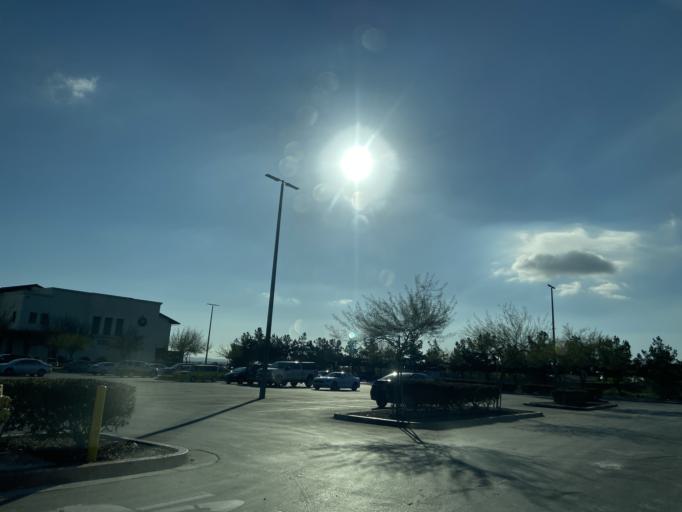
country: US
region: California
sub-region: San Diego County
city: Bonita
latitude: 32.6248
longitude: -116.9701
